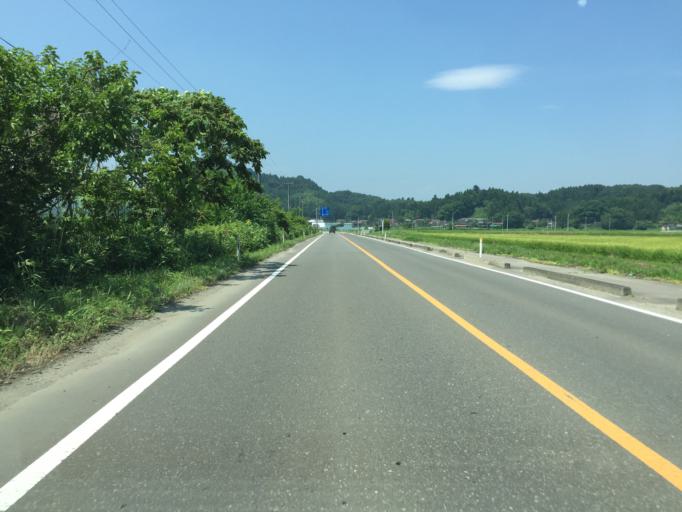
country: JP
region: Miyagi
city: Marumori
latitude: 37.8879
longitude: 140.8149
